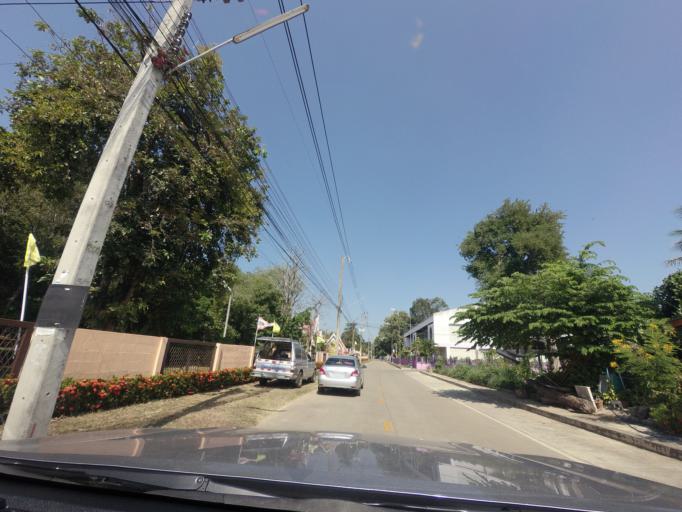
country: TH
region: Sukhothai
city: Sawankhalok
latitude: 17.3188
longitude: 99.8264
